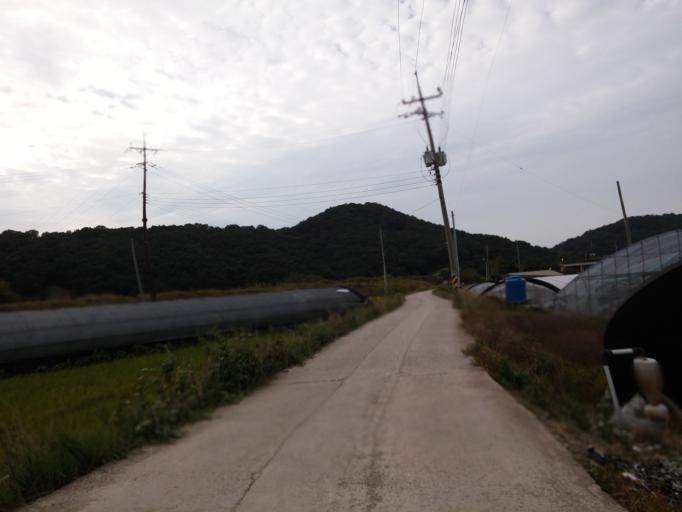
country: KR
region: Chungcheongnam-do
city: Yonmu
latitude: 36.1555
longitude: 127.2048
